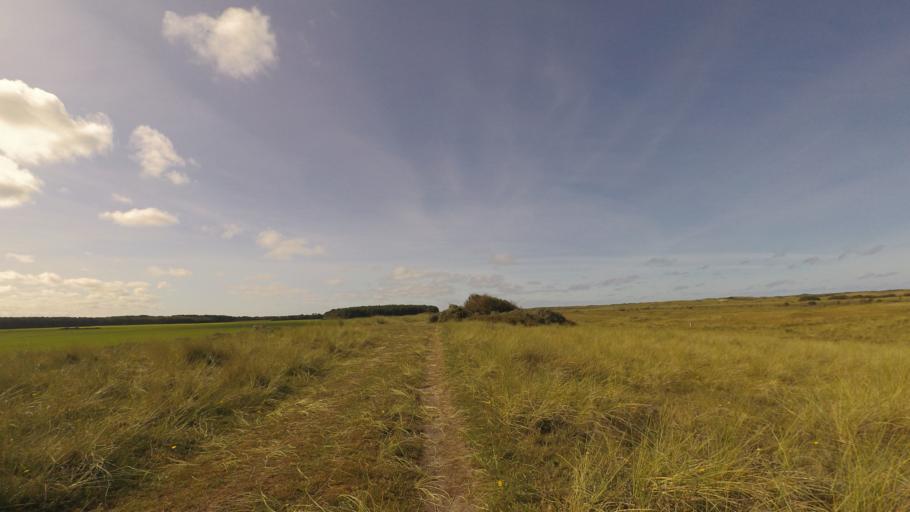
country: NL
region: Friesland
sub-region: Gemeente Ameland
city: Nes
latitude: 53.4503
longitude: 5.7262
